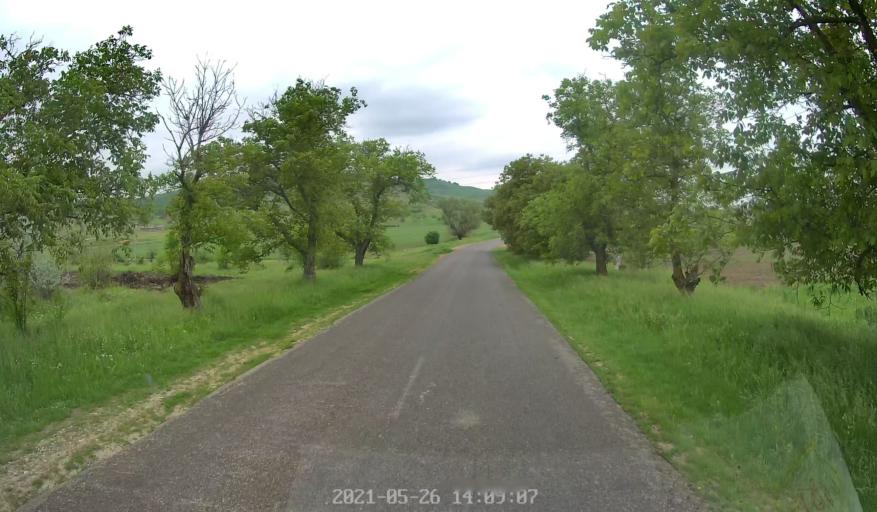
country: MD
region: Hincesti
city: Dancu
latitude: 46.7316
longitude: 28.3603
